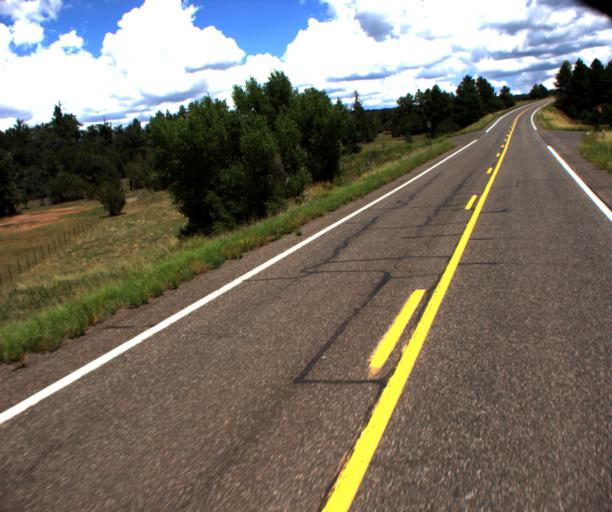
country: US
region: Arizona
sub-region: Gila County
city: Pine
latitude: 34.5029
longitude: -111.5774
